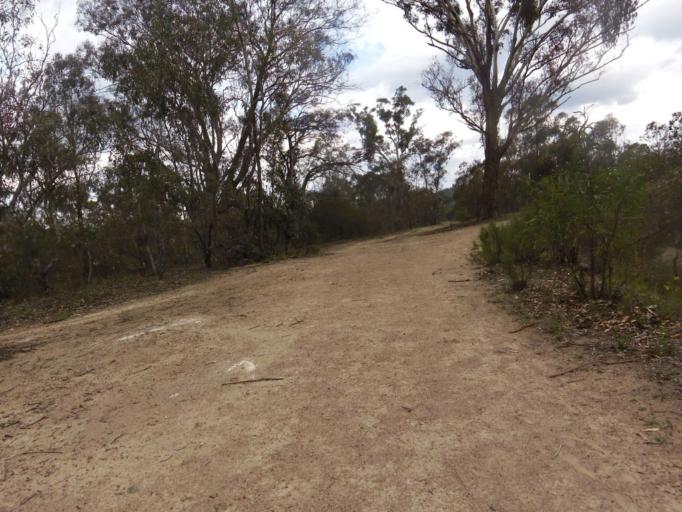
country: AU
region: Australian Capital Territory
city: Forrest
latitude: -35.3562
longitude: 149.1139
